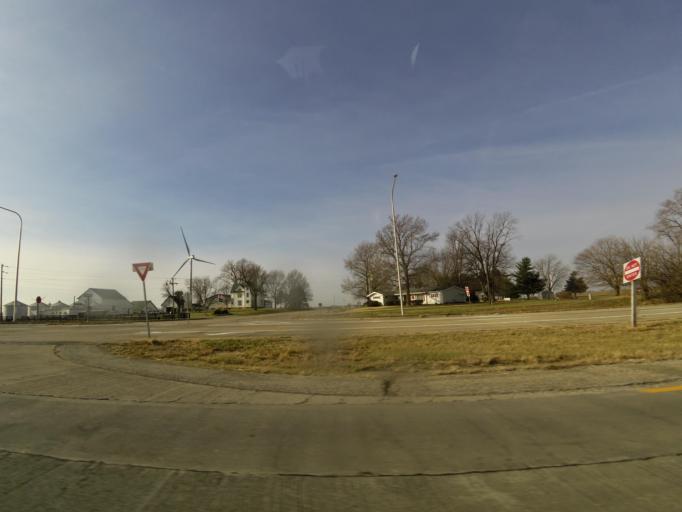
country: US
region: Illinois
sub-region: Macon County
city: Maroa
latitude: 40.0371
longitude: -88.9650
